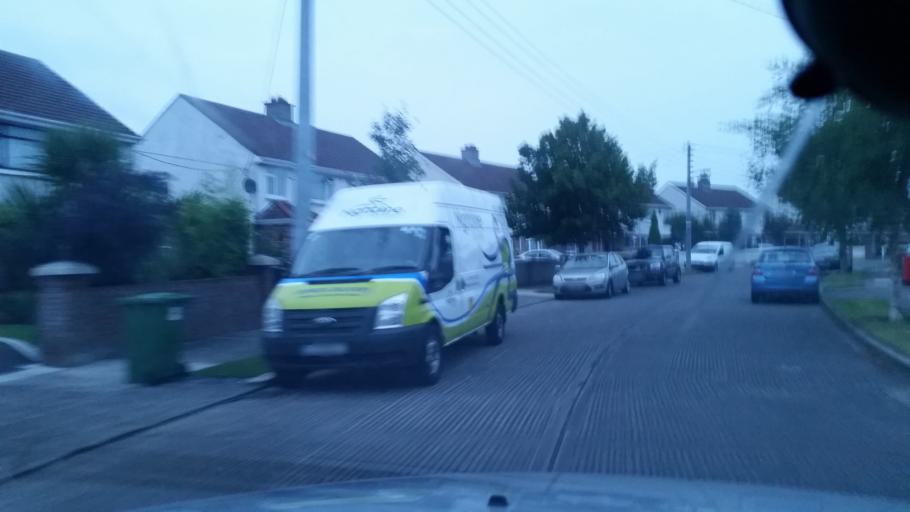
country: IE
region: Leinster
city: Beaumont
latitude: 53.3931
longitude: -6.2362
